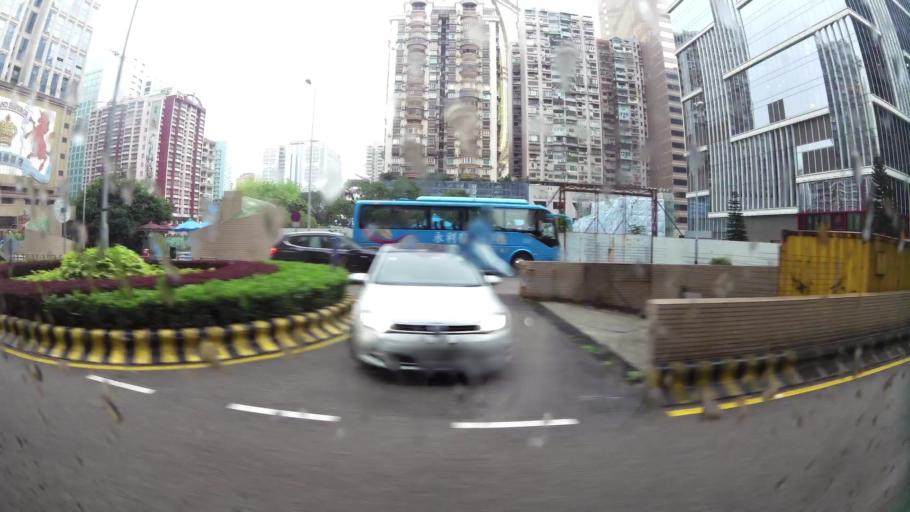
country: MO
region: Macau
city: Macau
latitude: 22.1897
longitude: 113.5412
